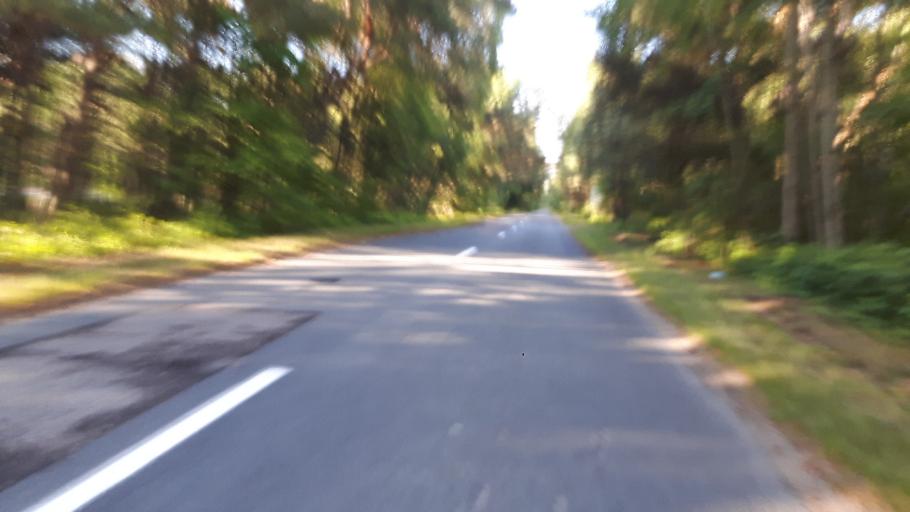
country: LT
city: Nida
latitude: 55.2405
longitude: 20.9142
